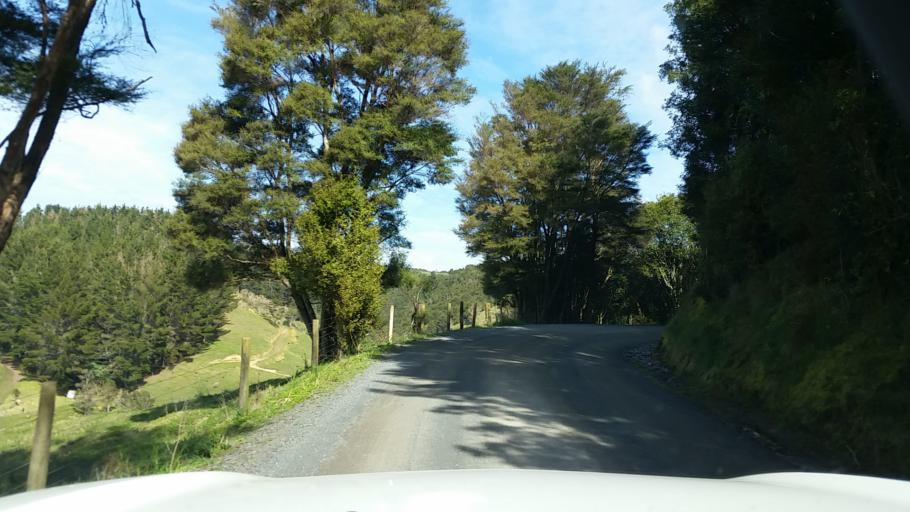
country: NZ
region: Waikato
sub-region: Hauraki District
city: Ngatea
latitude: -37.4477
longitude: 175.4839
